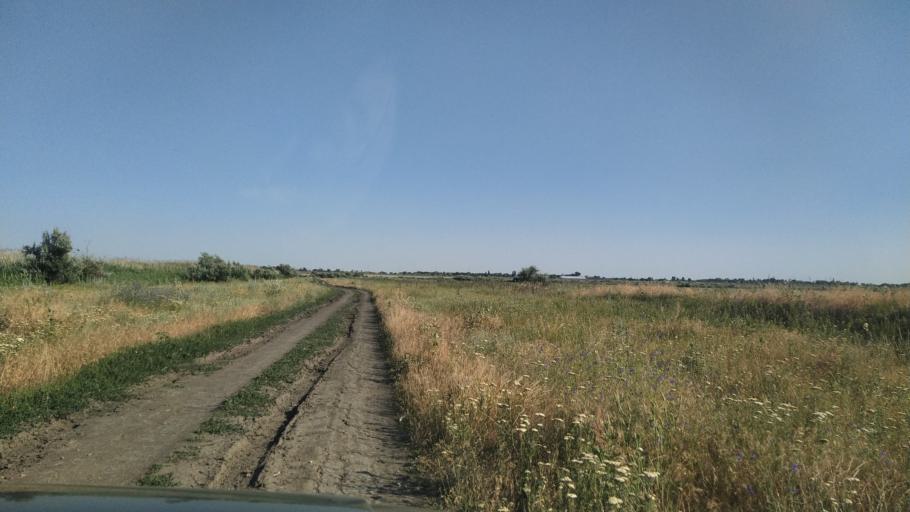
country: RU
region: Rostov
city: Kuleshovka
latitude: 47.1243
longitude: 39.6471
